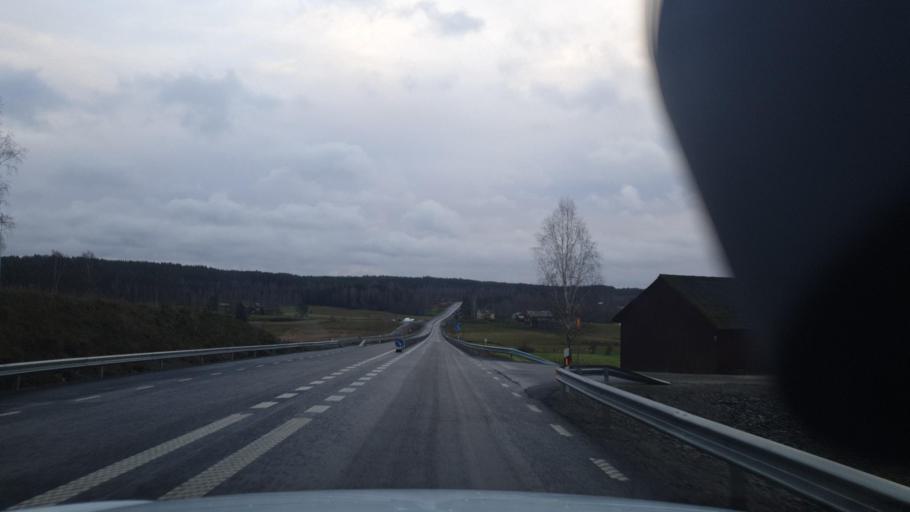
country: SE
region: Vaermland
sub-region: Arvika Kommun
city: Arvika
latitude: 59.7094
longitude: 12.5489
